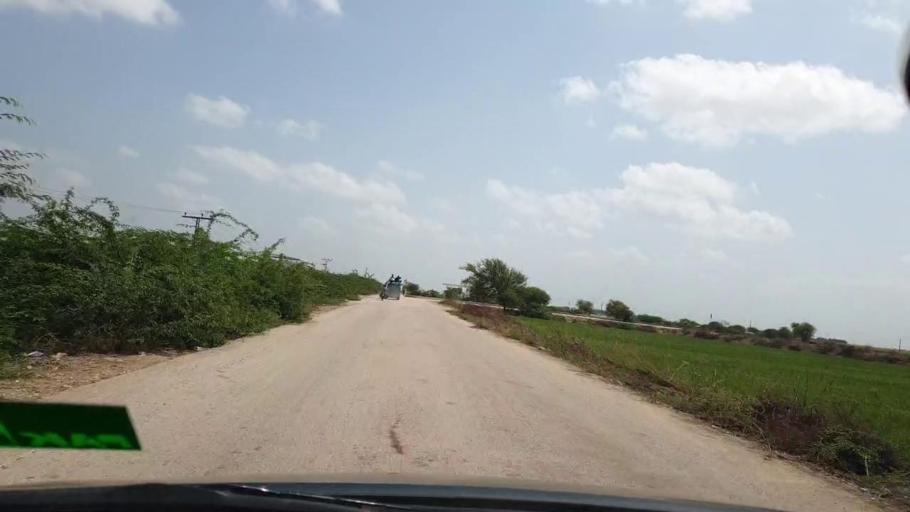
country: PK
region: Sindh
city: Kadhan
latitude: 24.6275
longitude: 69.1878
